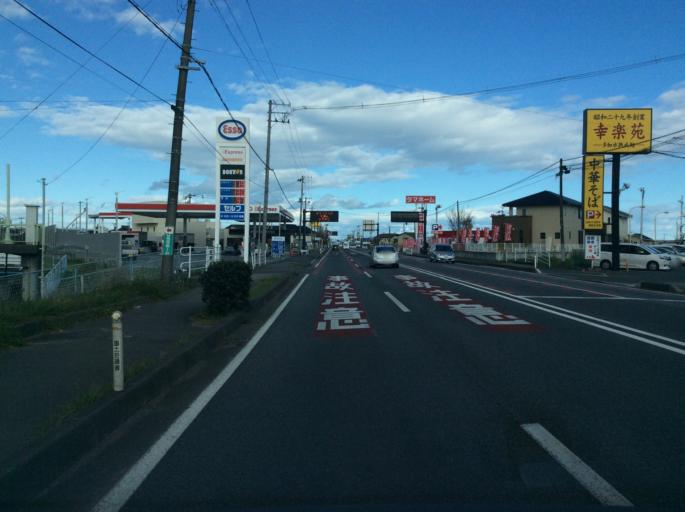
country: JP
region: Fukushima
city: Iwaki
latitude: 37.0665
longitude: 140.9446
